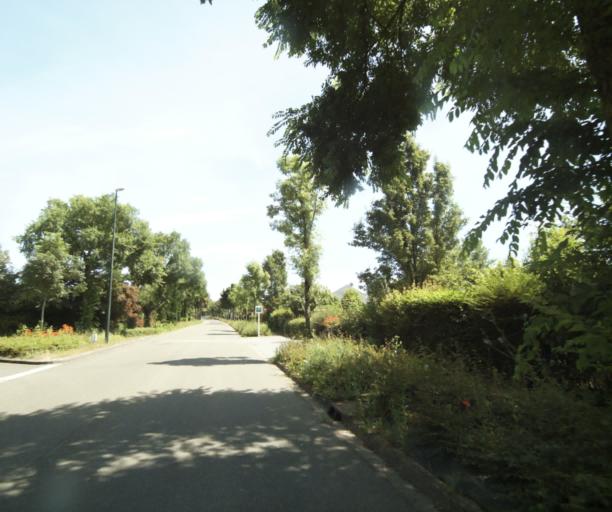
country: FR
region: Pays de la Loire
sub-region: Departement de la Mayenne
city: Change
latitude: 48.0808
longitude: -0.8090
